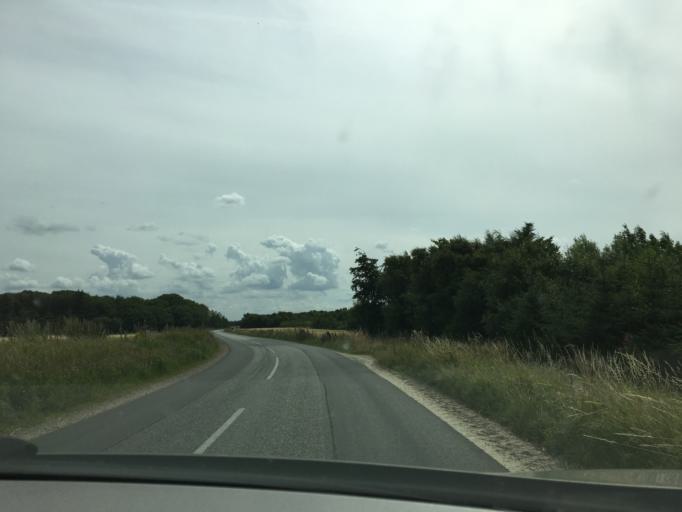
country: DK
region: Central Jutland
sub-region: Ringkobing-Skjern Kommune
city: Ringkobing
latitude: 55.9854
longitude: 8.3402
